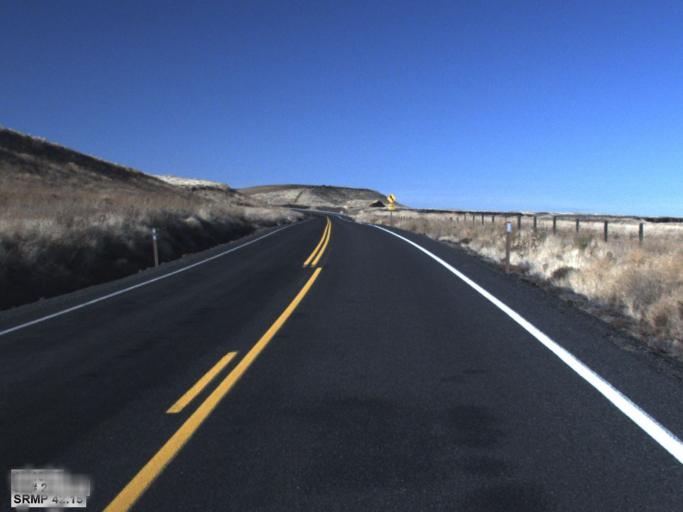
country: US
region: Washington
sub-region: Adams County
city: Ritzville
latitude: 46.8313
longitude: -118.3265
